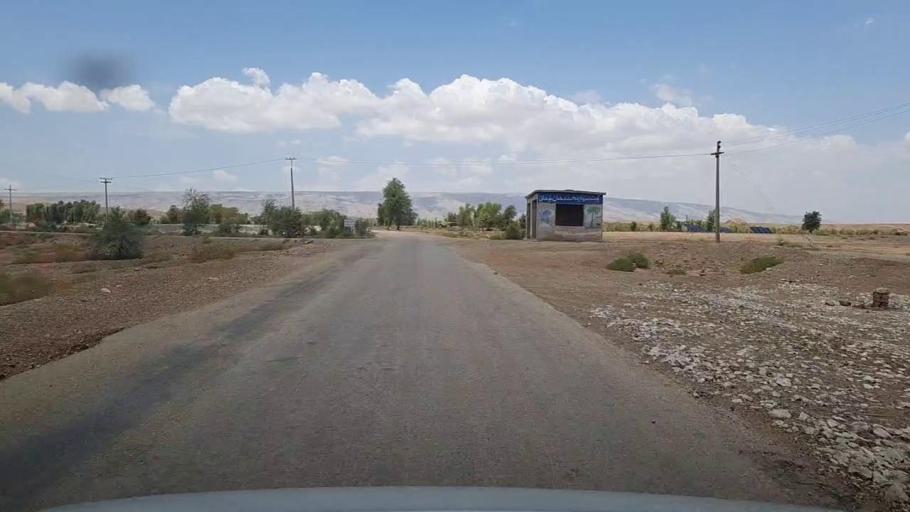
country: PK
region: Sindh
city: Bhan
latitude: 26.3163
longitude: 67.5827
